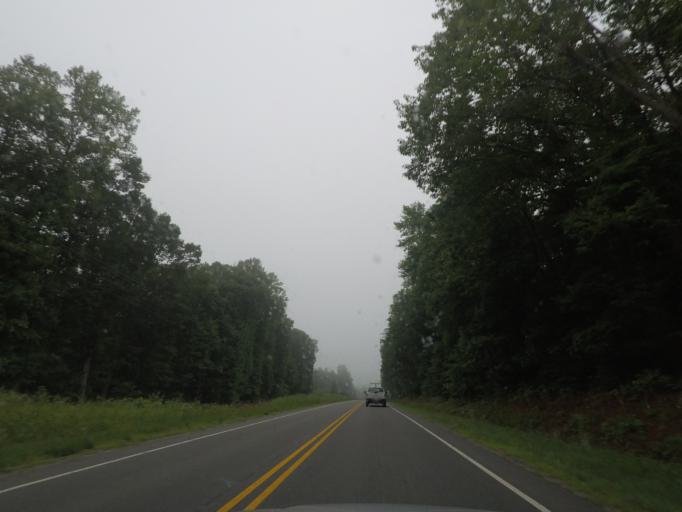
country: US
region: Virginia
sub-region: Buckingham County
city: Buckingham
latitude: 37.4717
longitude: -78.4708
